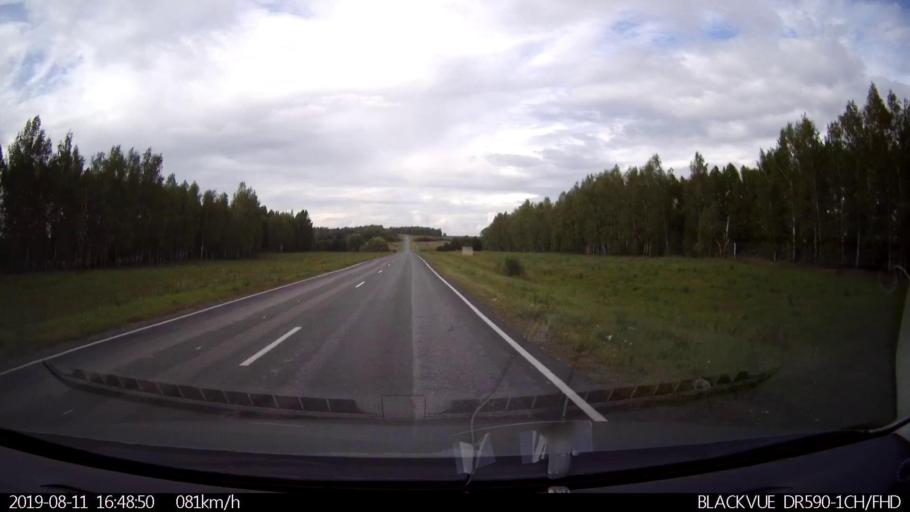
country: RU
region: Ulyanovsk
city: Mayna
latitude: 54.2140
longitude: 47.6937
